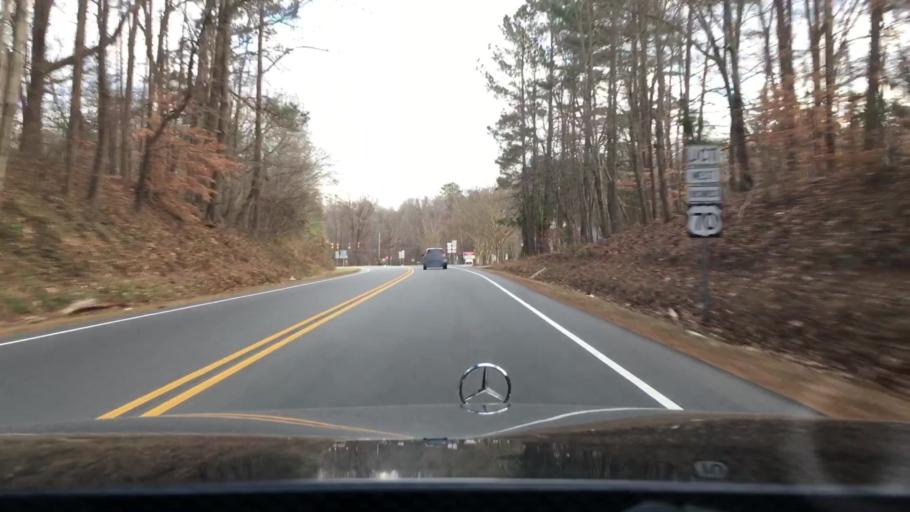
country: US
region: North Carolina
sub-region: Orange County
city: Hillsborough
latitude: 36.0578
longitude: -79.0515
